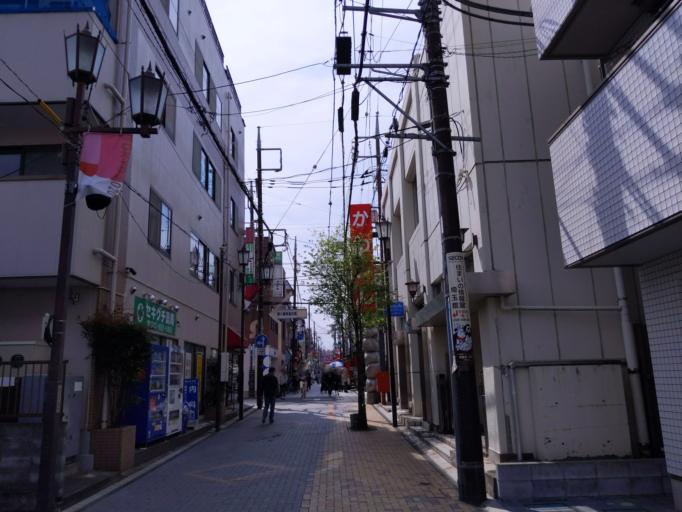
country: JP
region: Saitama
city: Yono
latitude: 35.8718
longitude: 139.6421
